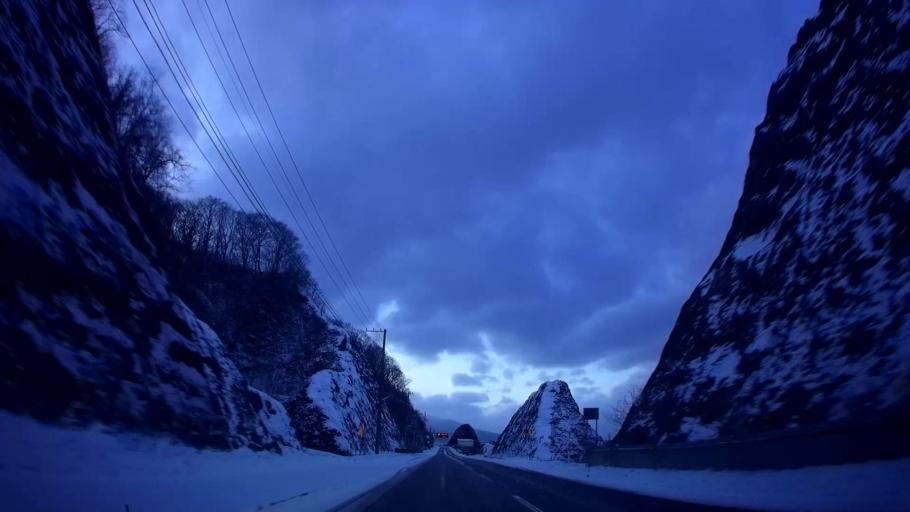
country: JP
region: Hokkaido
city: Hakodate
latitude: 41.8915
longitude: 141.0508
